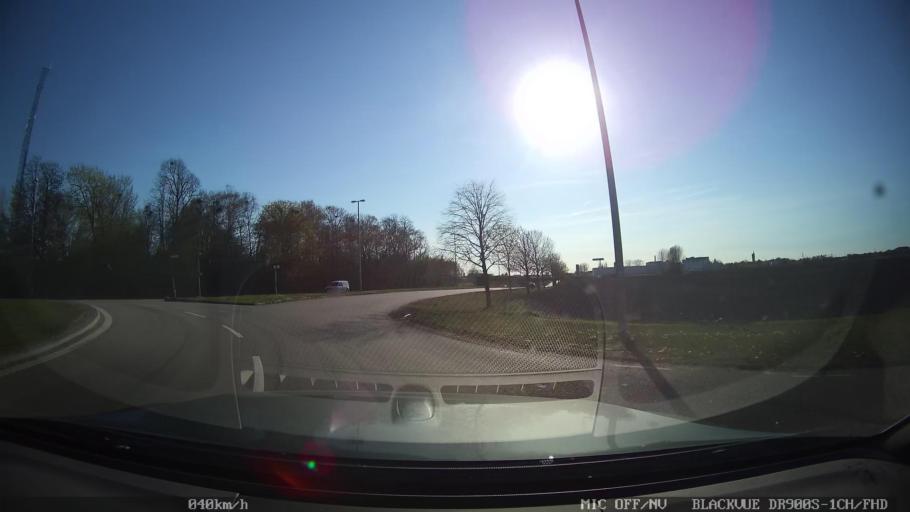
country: SE
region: Skane
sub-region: Landskrona
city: Landskrona
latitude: 55.8741
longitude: 12.8677
